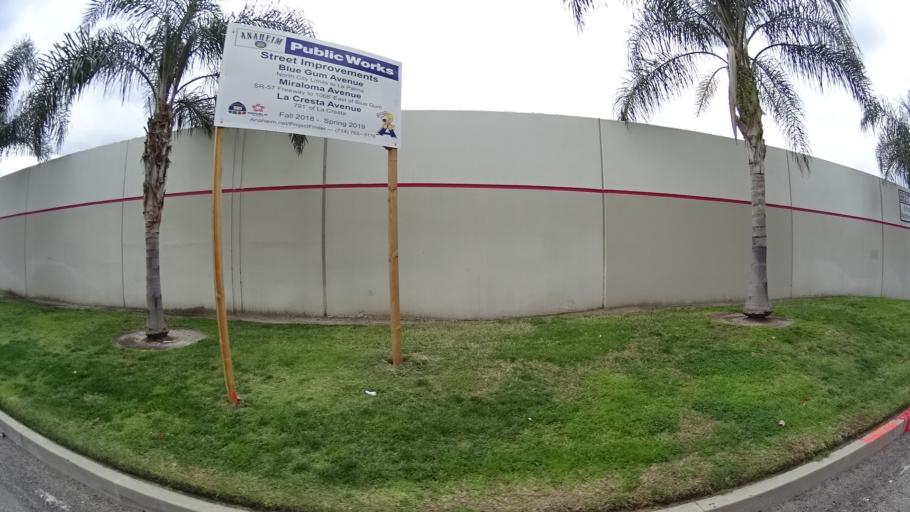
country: US
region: California
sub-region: Orange County
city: Placentia
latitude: 33.8578
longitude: -117.8734
